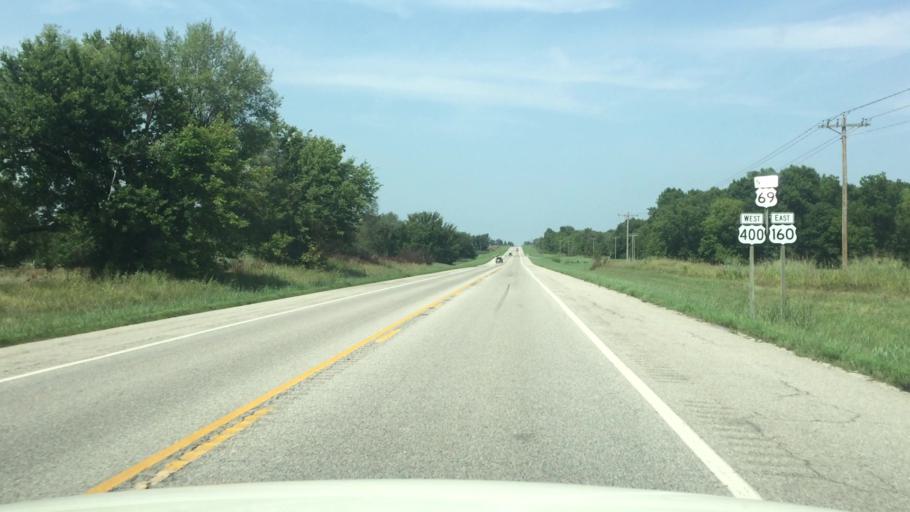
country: US
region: Missouri
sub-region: Jasper County
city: Carl Junction
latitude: 37.2517
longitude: -94.7051
